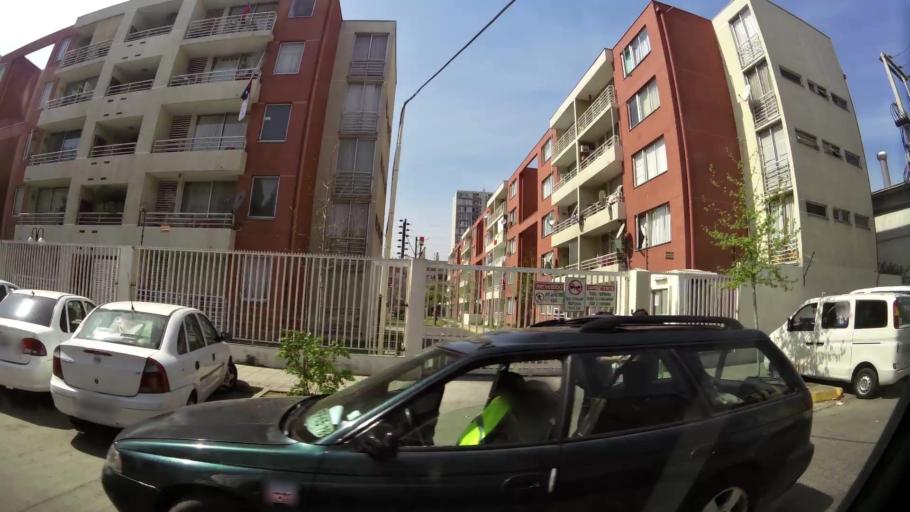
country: CL
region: Santiago Metropolitan
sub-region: Provincia de Santiago
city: Lo Prado
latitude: -33.4259
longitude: -70.6862
